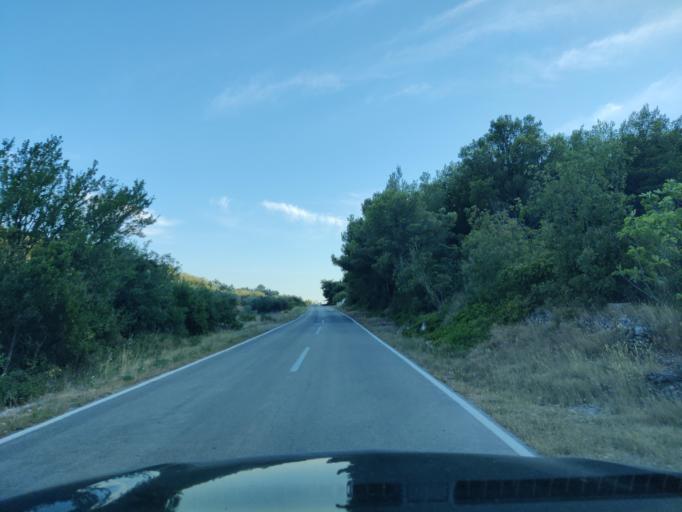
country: HR
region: Sibensko-Kniniska
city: Tribunj
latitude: 43.7894
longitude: 15.7283
